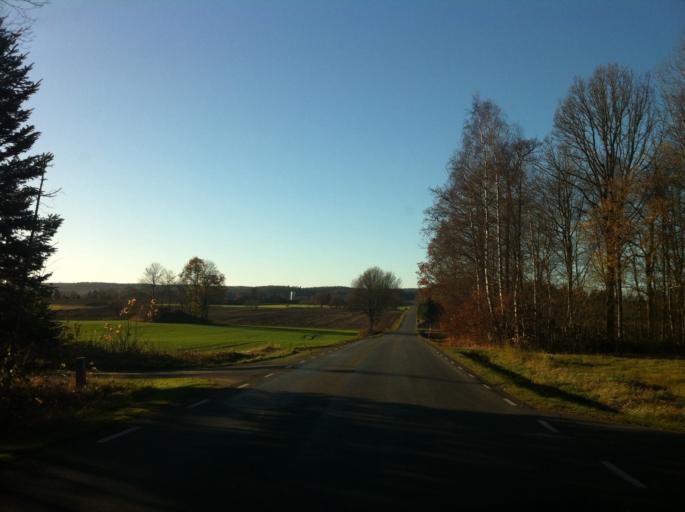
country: SE
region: Blekinge
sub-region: Olofstroms Kommun
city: Jamshog
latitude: 56.1793
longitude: 14.5521
